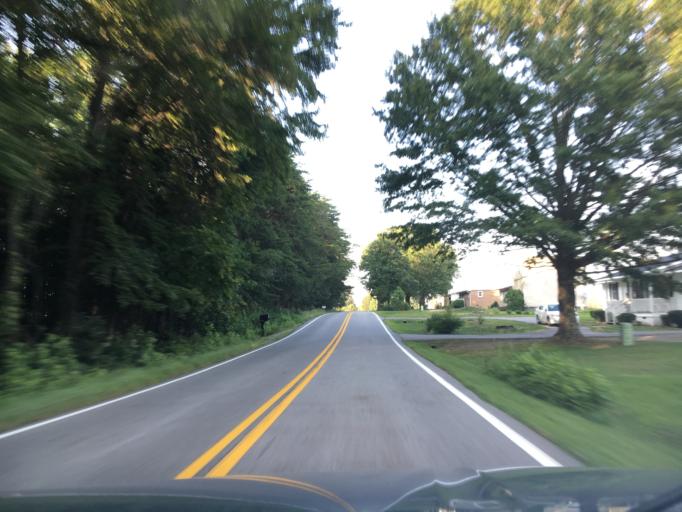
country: US
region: Virginia
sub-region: Pittsylvania County
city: Chatham
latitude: 36.8185
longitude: -79.2595
